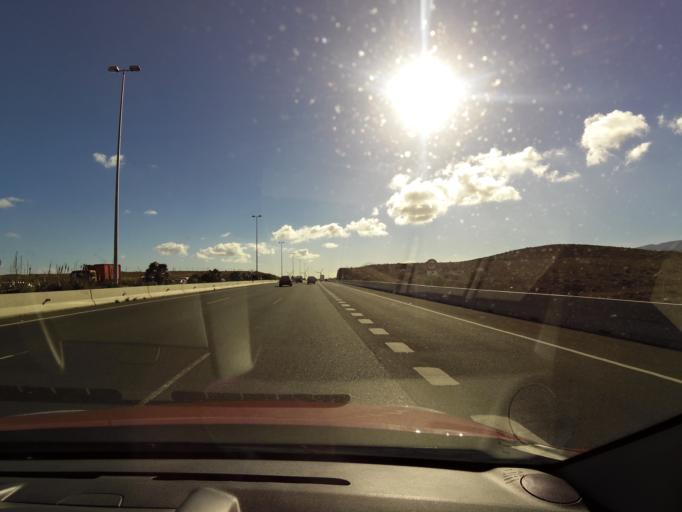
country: ES
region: Canary Islands
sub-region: Provincia de Las Palmas
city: Cruce de Arinaga
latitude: 27.8819
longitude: -15.4116
